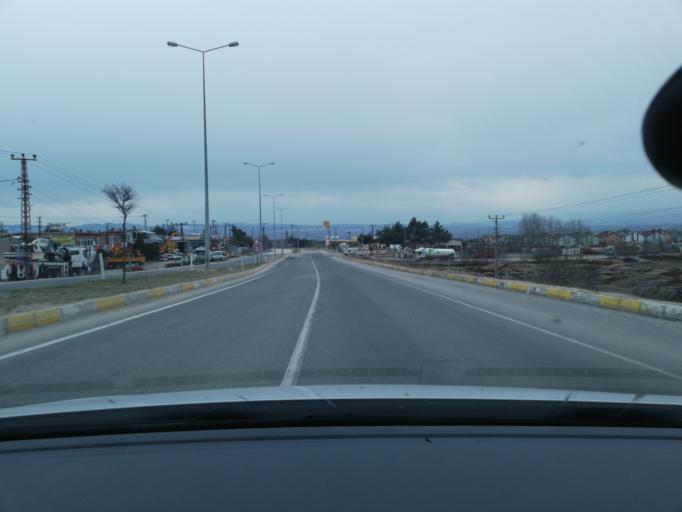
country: TR
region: Bolu
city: Gerede
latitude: 40.7894
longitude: 32.2085
